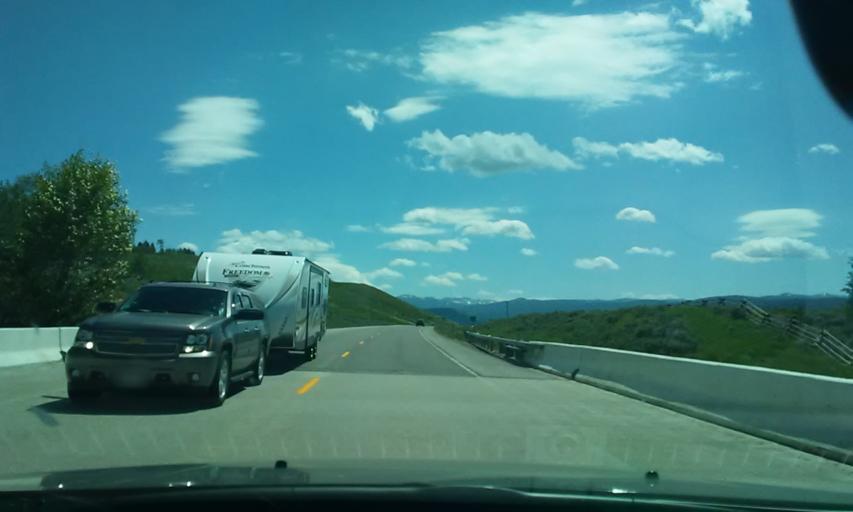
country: US
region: Wyoming
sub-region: Teton County
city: Jackson
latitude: 43.8402
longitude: -110.4573
